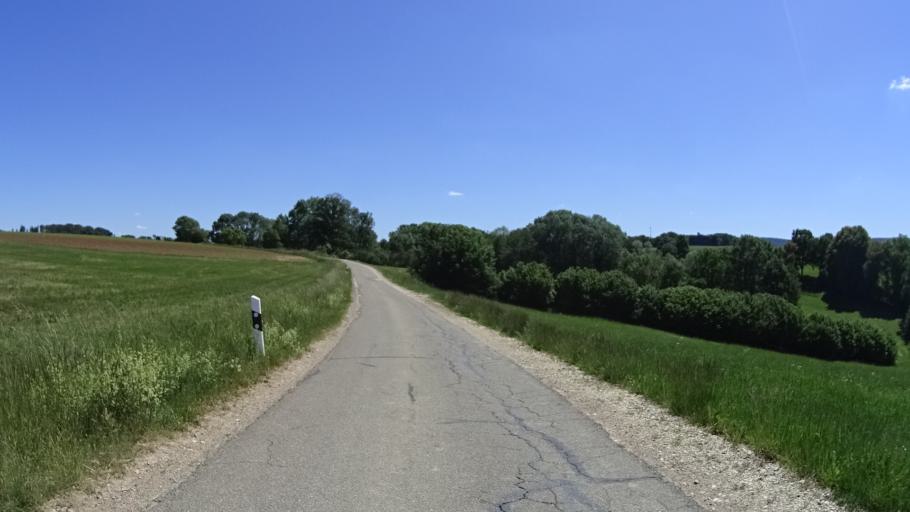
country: DE
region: Bavaria
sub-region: Regierungsbezirk Mittelfranken
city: Hottingen
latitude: 49.0820
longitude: 10.9974
